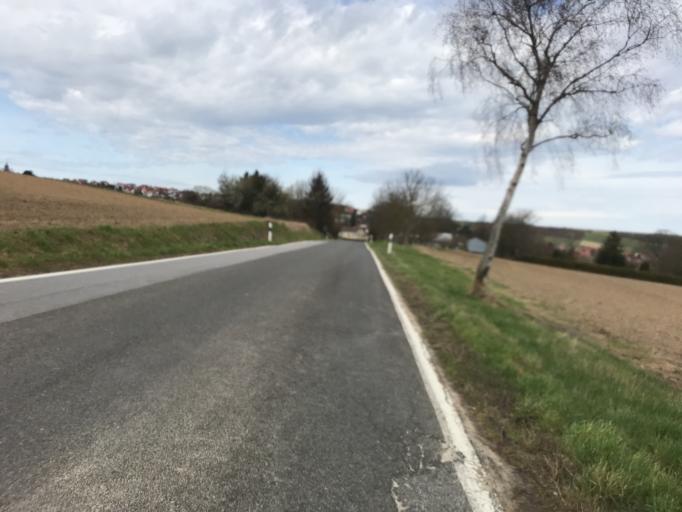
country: DE
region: Rheinland-Pfalz
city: Partenheim
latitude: 49.8819
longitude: 8.0865
